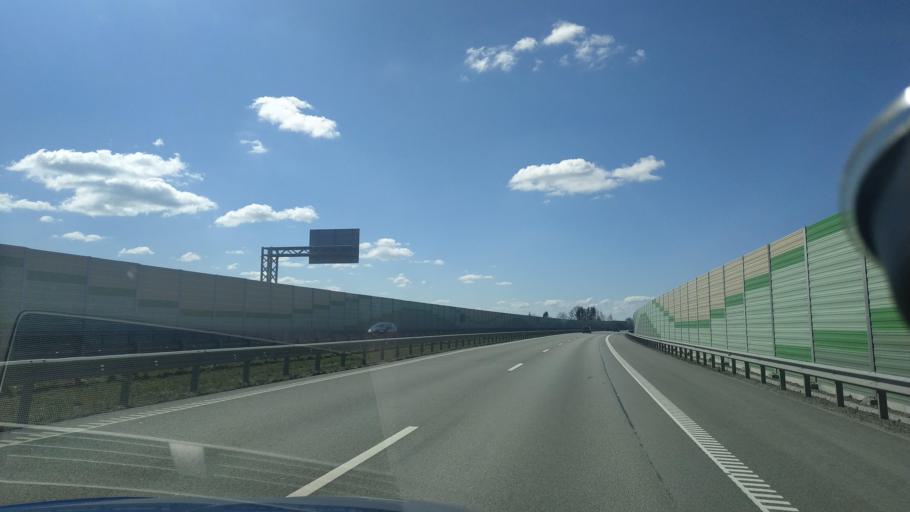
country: LT
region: Kauno apskritis
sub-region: Kauno rajonas
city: Mastaiciai
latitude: 54.7759
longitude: 23.7756
